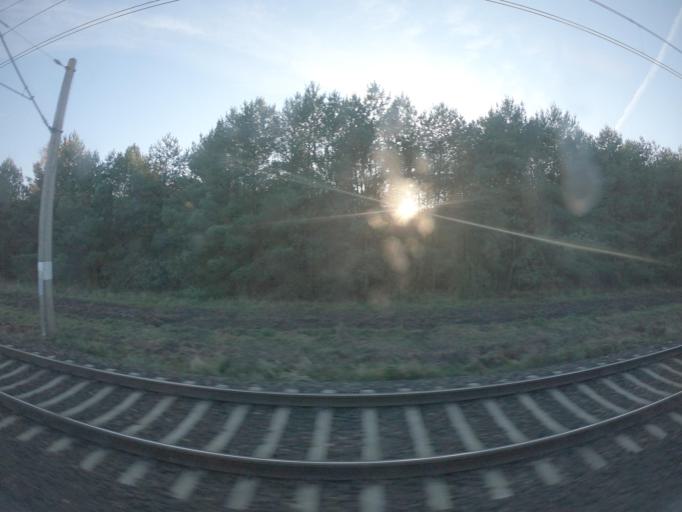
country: PL
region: Lubusz
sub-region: Powiat slubicki
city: Rzepin
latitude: 52.2731
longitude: 14.9197
